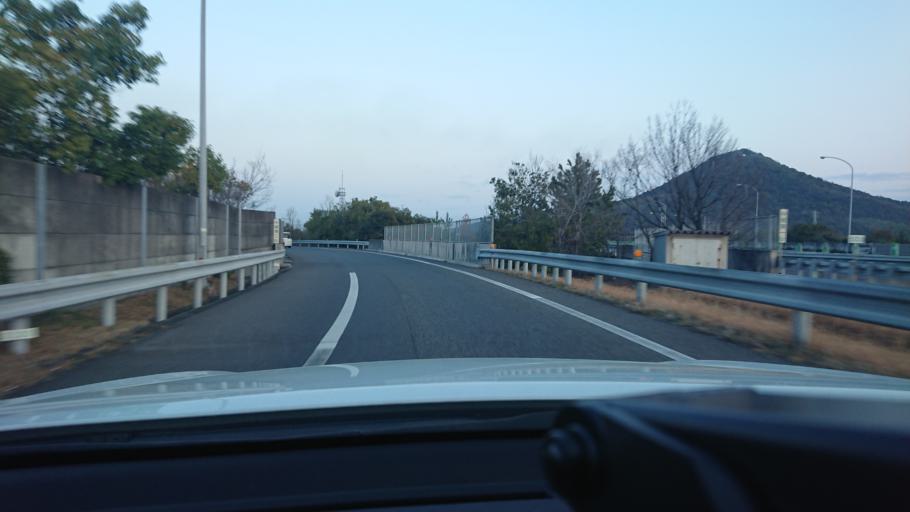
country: JP
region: Kagawa
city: Sakaidecho
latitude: 34.2936
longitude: 133.8475
